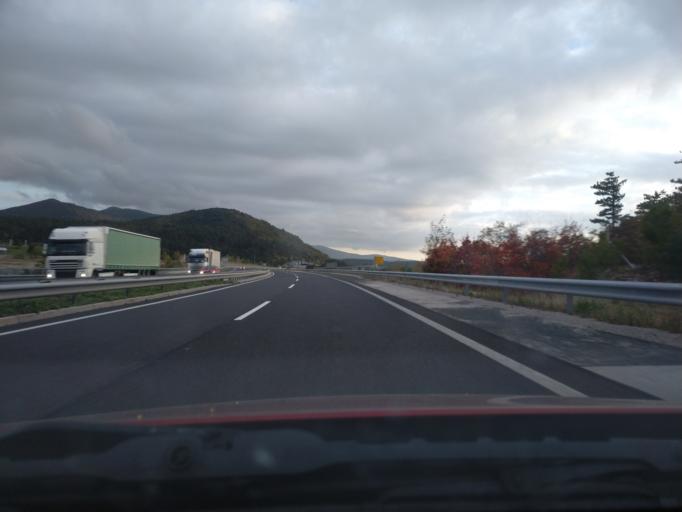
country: SI
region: Hrpelje-Kozina
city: Kozina
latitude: 45.6030
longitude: 13.9279
